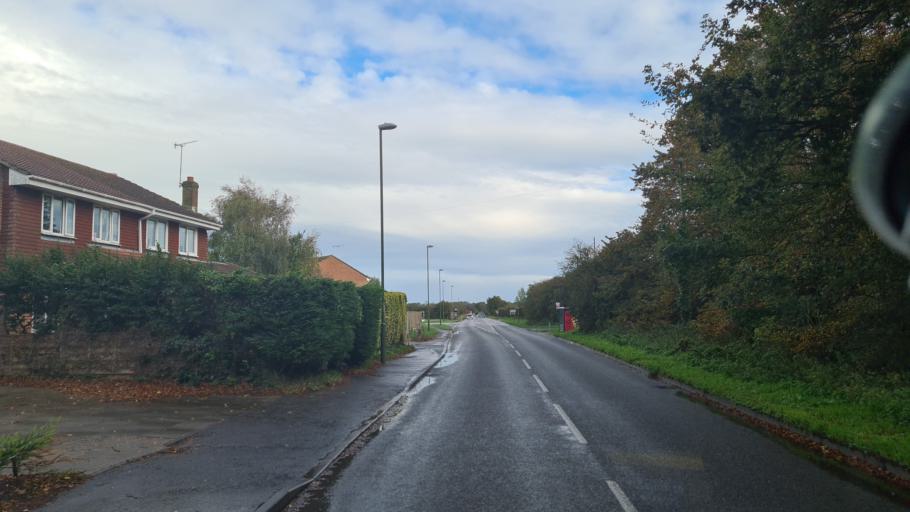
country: GB
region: England
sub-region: West Sussex
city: Walberton
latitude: 50.8163
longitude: -0.5997
